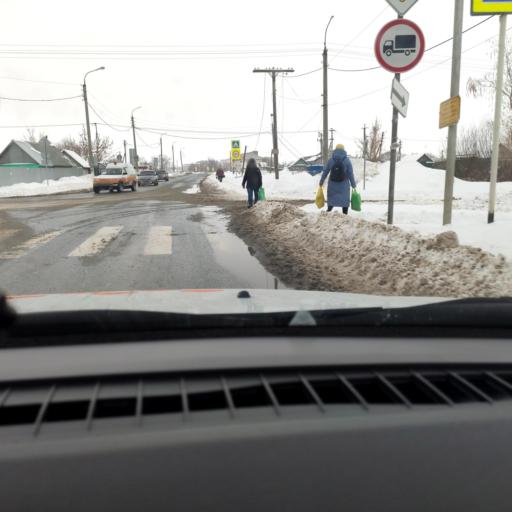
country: RU
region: Saratov
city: Perelyub
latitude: 52.0985
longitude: 50.8668
